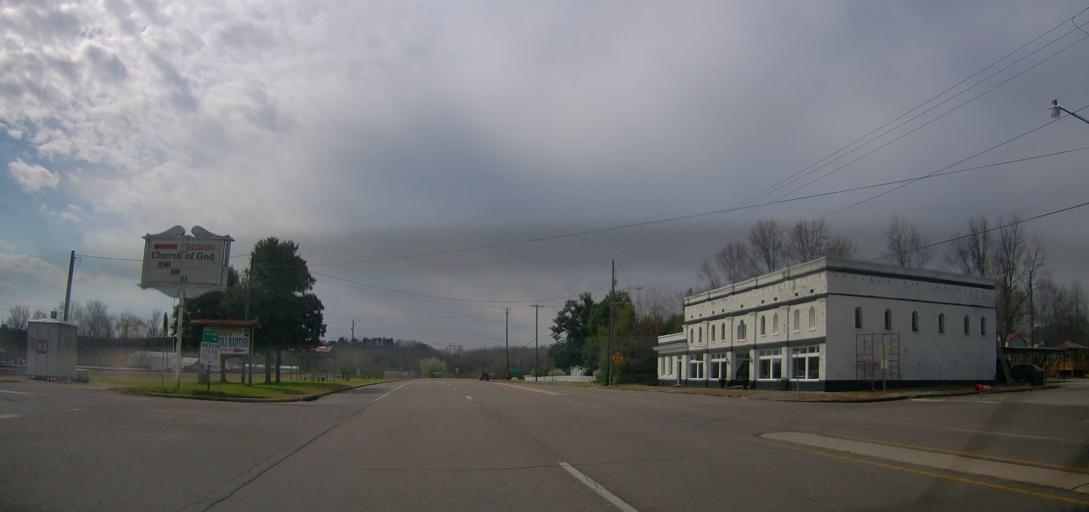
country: US
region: Alabama
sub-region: Walker County
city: Carbon Hill
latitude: 33.8892
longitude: -87.5310
